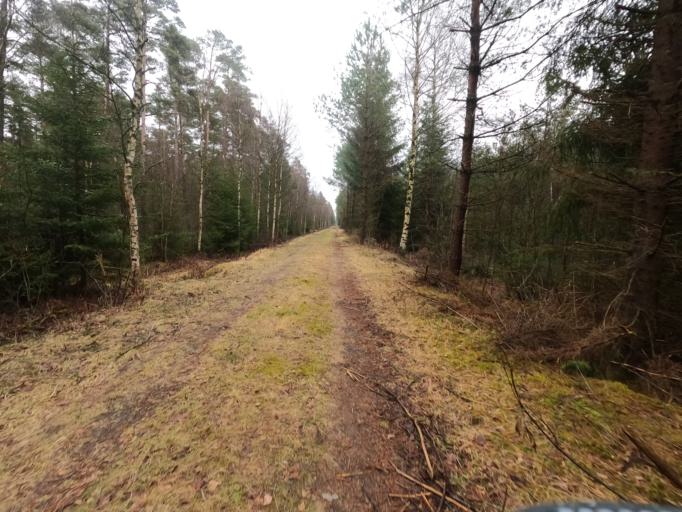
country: SE
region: Kronoberg
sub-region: Markaryds Kommun
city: Stromsnasbruk
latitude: 56.7915
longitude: 13.5804
